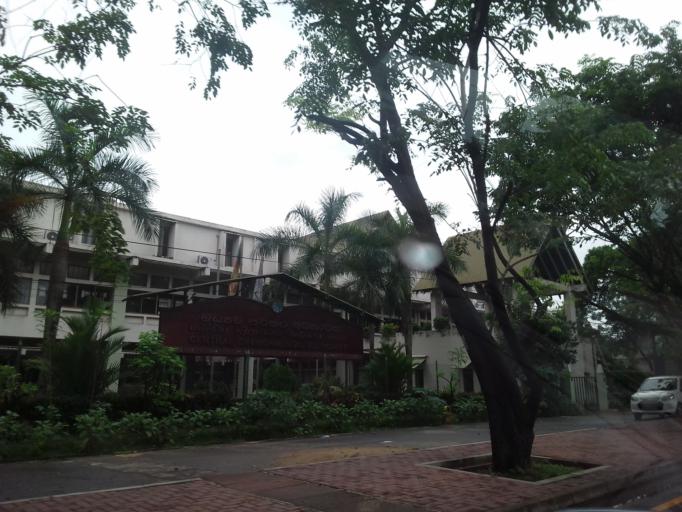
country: LK
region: Western
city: Battaramulla South
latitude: 6.9000
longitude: 79.9269
